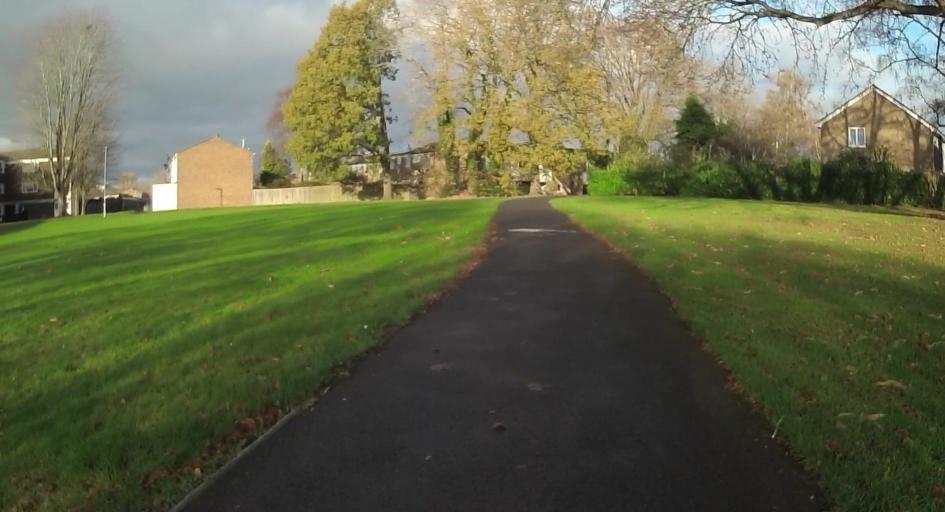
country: GB
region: England
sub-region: Bracknell Forest
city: Bracknell
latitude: 51.3949
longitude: -0.7696
